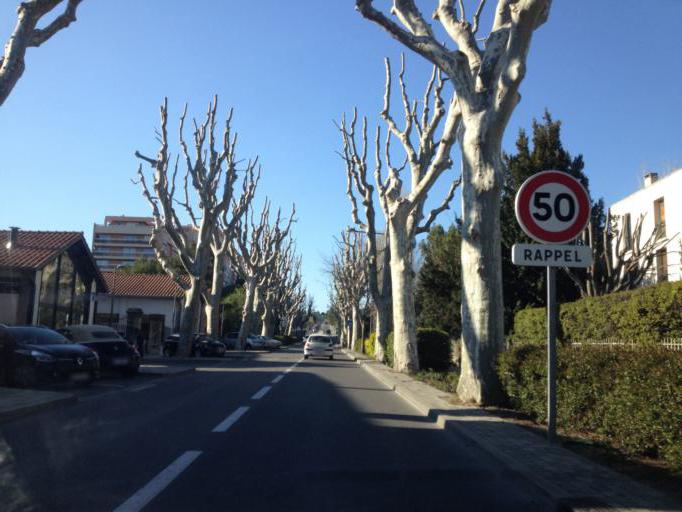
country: FR
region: Provence-Alpes-Cote d'Azur
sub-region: Departement des Bouches-du-Rhone
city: Aix-en-Provence
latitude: 43.5351
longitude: 5.4358
